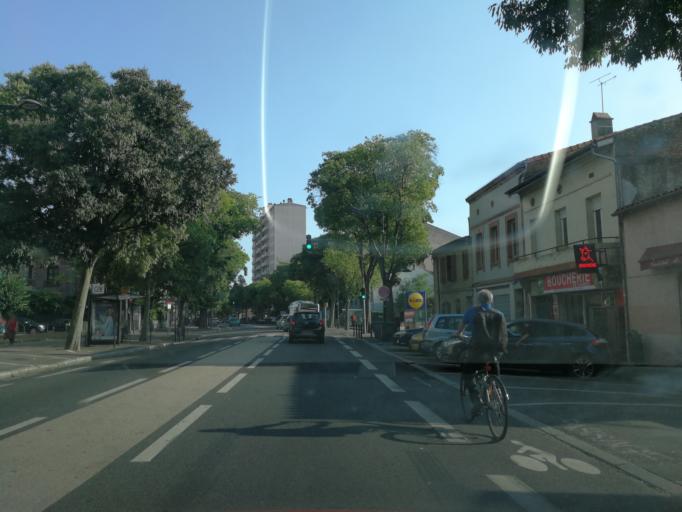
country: FR
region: Midi-Pyrenees
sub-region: Departement de la Haute-Garonne
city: Toulouse
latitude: 43.6239
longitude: 1.4343
